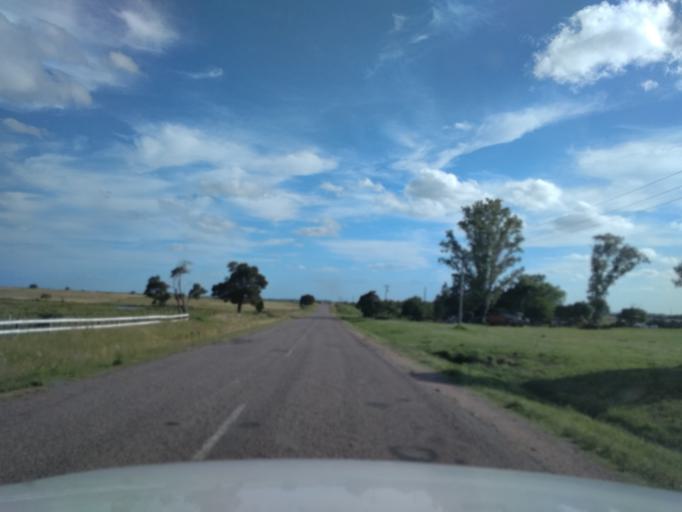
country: UY
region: Canelones
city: San Ramon
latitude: -34.2538
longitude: -55.9264
